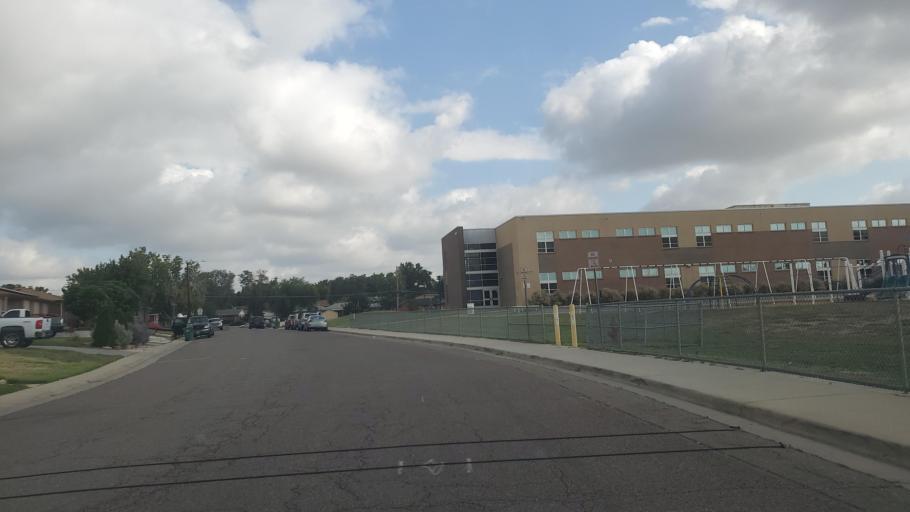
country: US
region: Colorado
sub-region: Adams County
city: Welby
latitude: 39.8476
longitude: -104.9708
